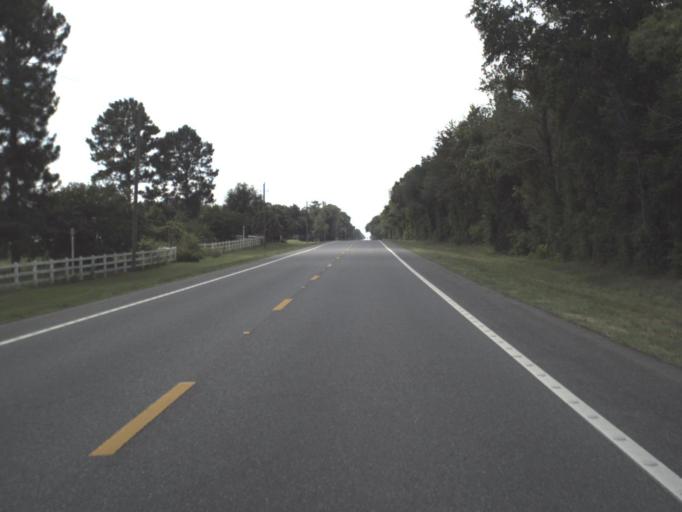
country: US
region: Florida
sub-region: Suwannee County
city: Wellborn
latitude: 30.1094
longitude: -82.9484
